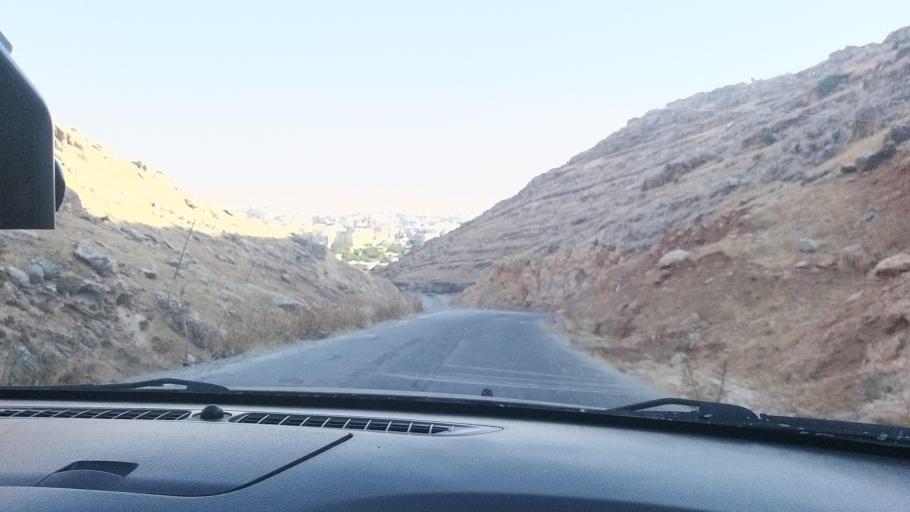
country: TR
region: Diyarbakir
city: Silvan
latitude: 38.1582
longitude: 41.0031
